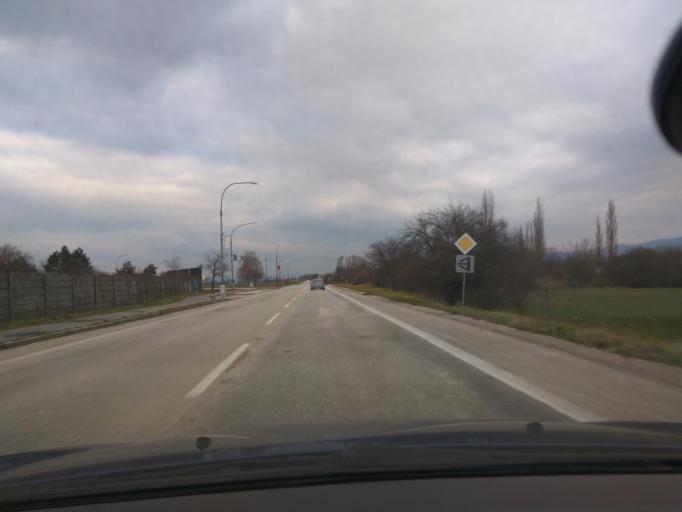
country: SK
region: Trnavsky
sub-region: Okres Trnava
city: Piestany
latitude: 48.6097
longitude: 17.8335
